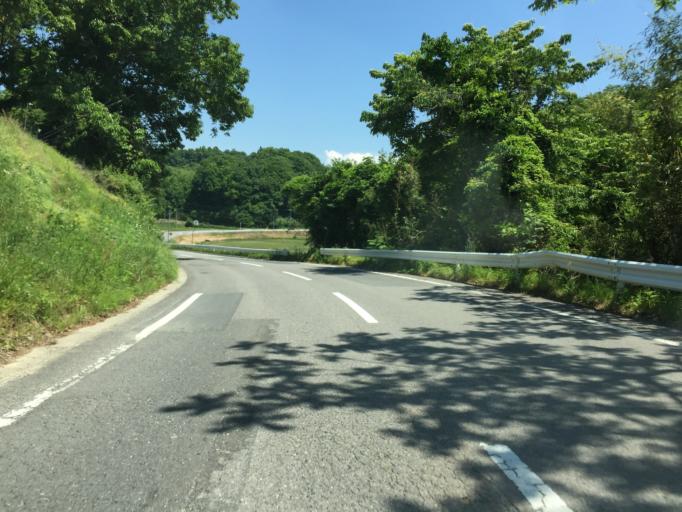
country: JP
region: Fukushima
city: Miharu
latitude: 37.4991
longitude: 140.4804
